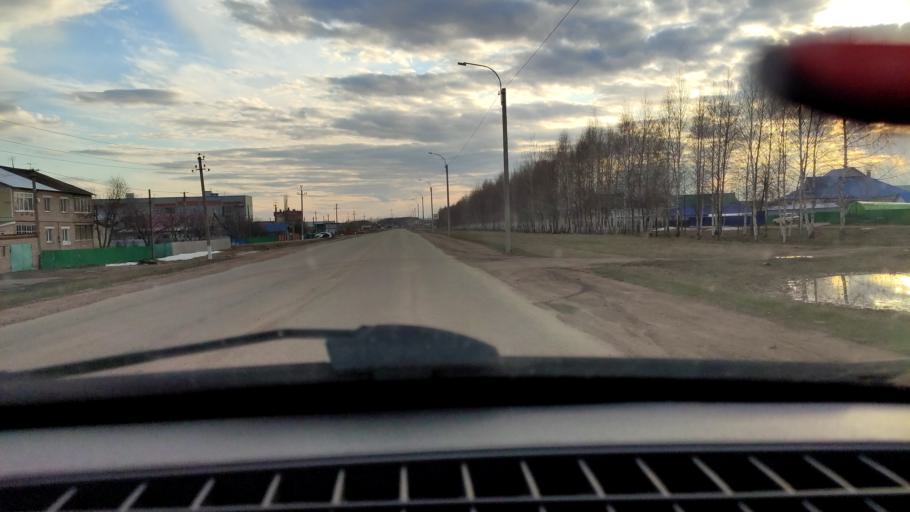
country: RU
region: Bashkortostan
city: Tolbazy
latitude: 54.0044
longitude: 55.8658
